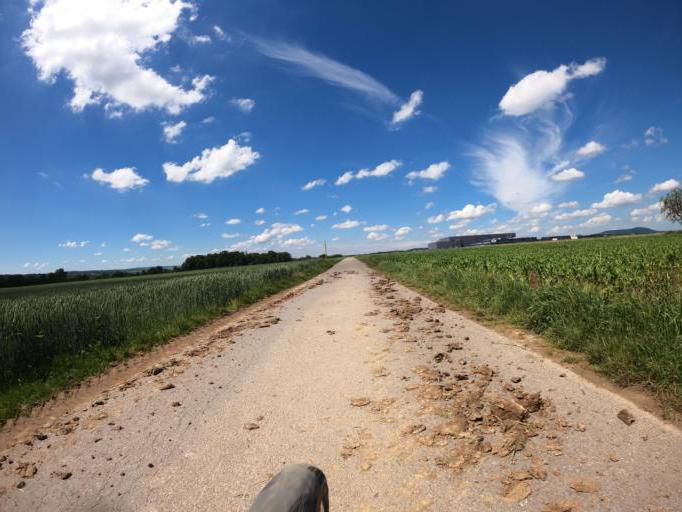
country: DE
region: Baden-Wuerttemberg
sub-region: Regierungsbezirk Stuttgart
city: Oberriexingen
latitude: 48.9473
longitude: 9.0611
